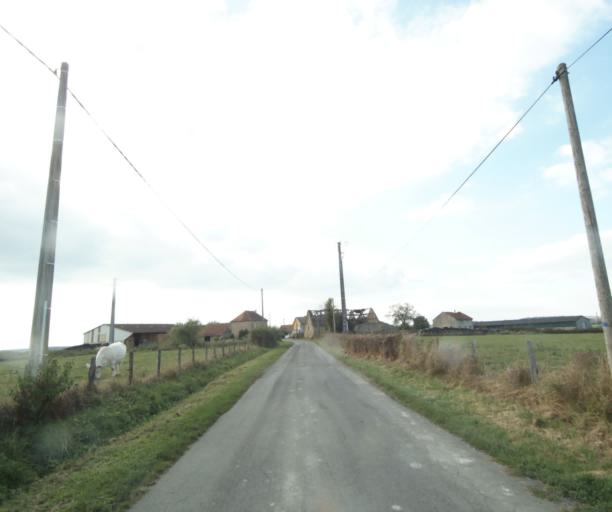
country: FR
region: Bourgogne
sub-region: Departement de Saone-et-Loire
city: Palinges
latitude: 46.5733
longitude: 4.1822
